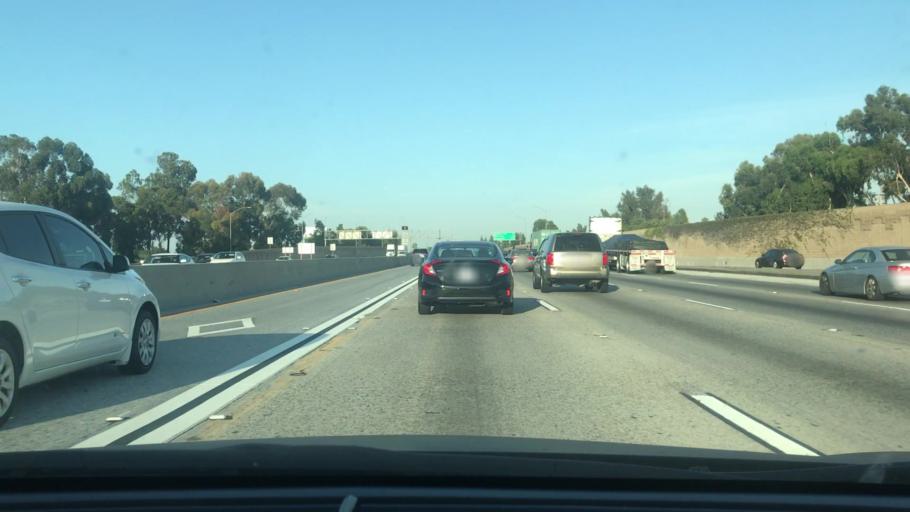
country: US
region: California
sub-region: Los Angeles County
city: Bellflower
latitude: 33.8767
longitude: -118.1389
